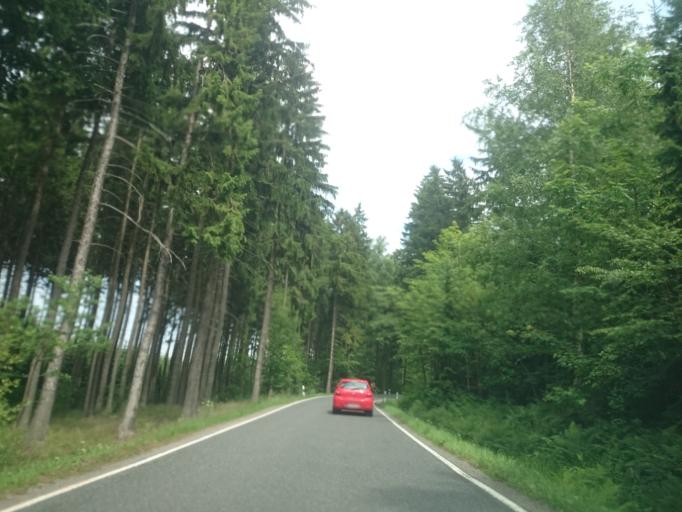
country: DE
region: Saxony
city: Augustusburg
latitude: 50.7899
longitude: 13.1000
